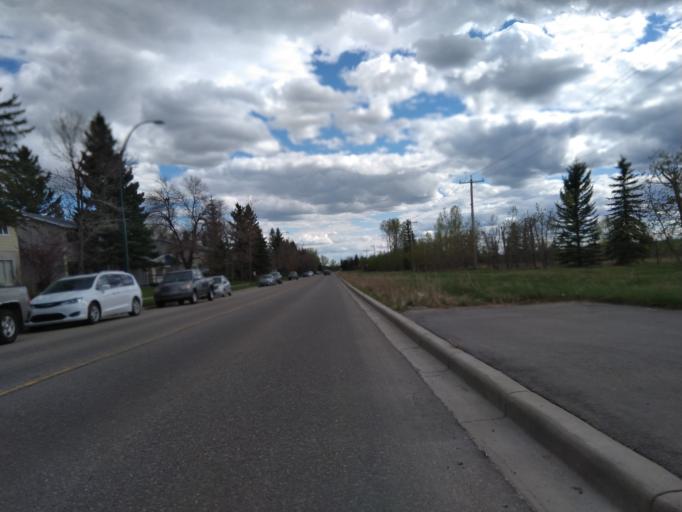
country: CA
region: Alberta
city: Calgary
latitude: 50.9984
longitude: -114.1411
